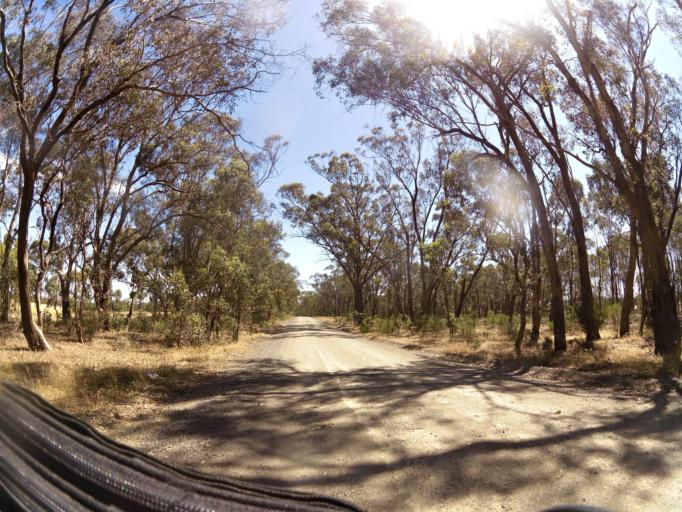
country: AU
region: Victoria
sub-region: Campaspe
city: Kyabram
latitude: -36.8400
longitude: 145.0724
